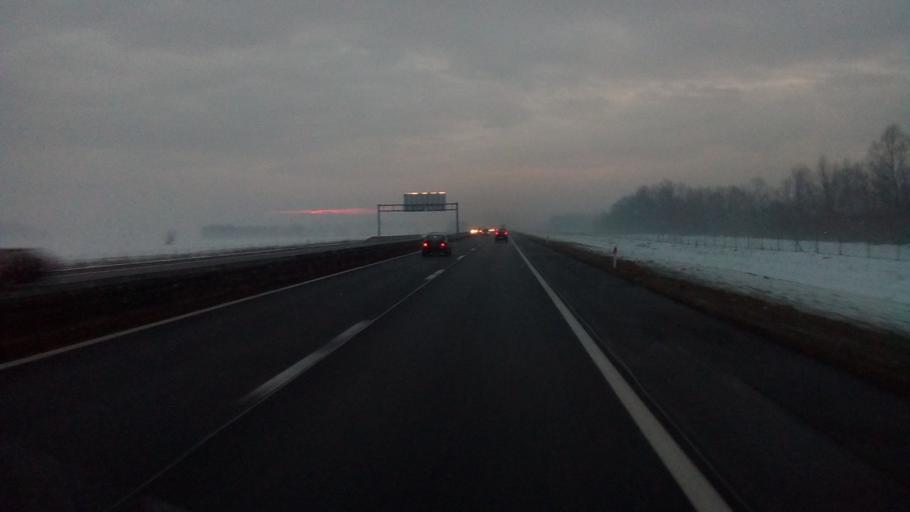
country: HR
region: Grad Zagreb
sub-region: Sesvete
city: Sesvete
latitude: 45.7832
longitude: 16.1875
